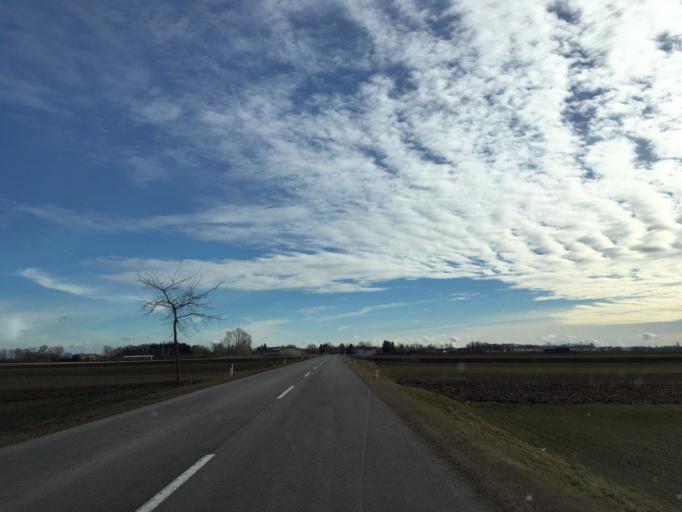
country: AT
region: Burgenland
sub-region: Politischer Bezirk Neusiedl am See
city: Pama
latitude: 48.0566
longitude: 17.0198
